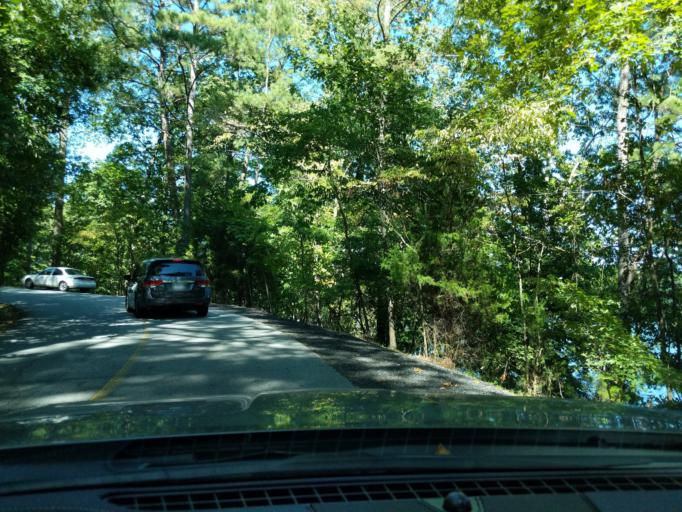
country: US
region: Georgia
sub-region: DeKalb County
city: Stone Mountain
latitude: 33.8051
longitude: -84.1340
